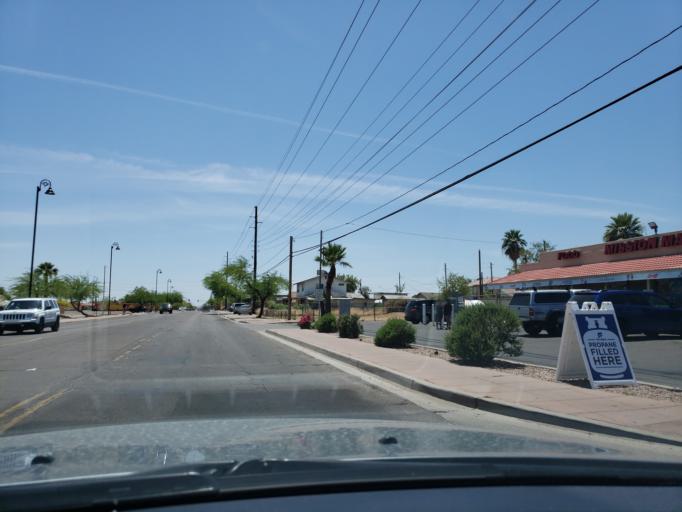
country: US
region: Arizona
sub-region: Maricopa County
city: Guadalupe
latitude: 33.3670
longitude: -111.9632
